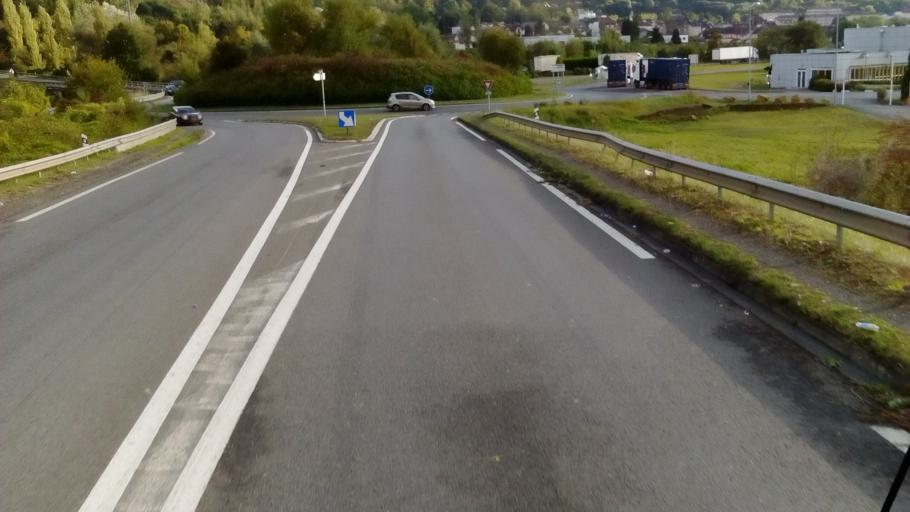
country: FR
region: Lorraine
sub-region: Departement de Meurthe-et-Moselle
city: Longlaville
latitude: 49.5419
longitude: 5.8076
